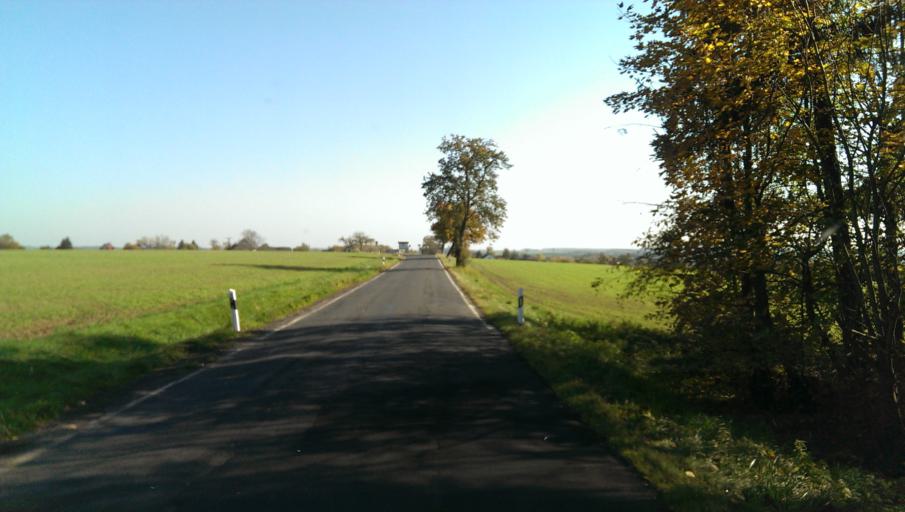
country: DE
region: Saxony
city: Kriebstein
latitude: 51.0356
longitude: 12.9833
